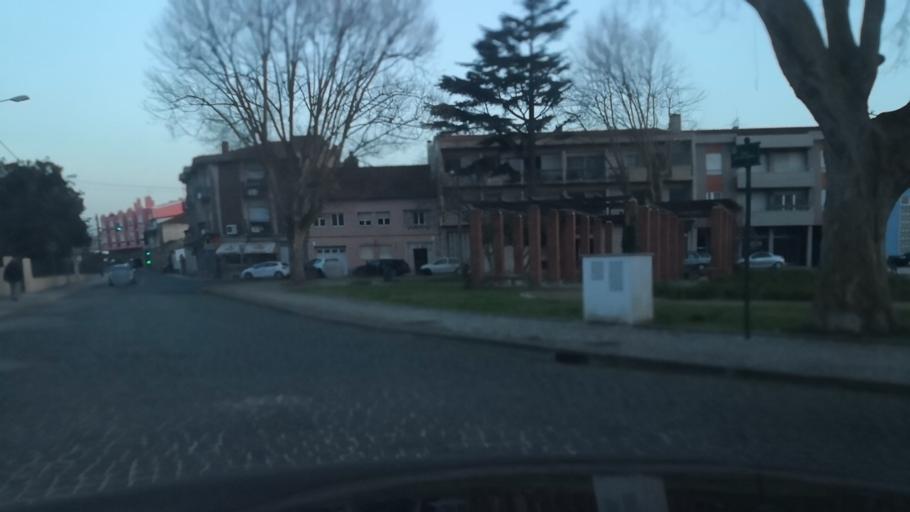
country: PT
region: Leiria
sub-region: Marinha Grande
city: Marinha Grande
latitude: 39.7514
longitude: -8.9289
